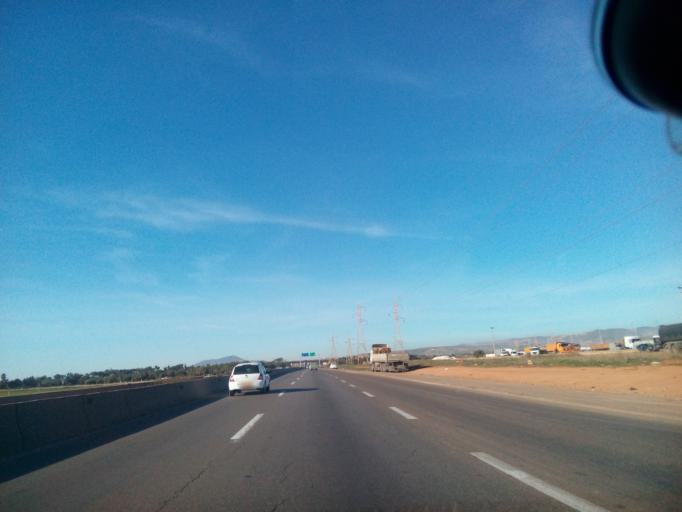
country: DZ
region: Oran
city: Ain el Bya
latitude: 35.7998
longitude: -0.3408
